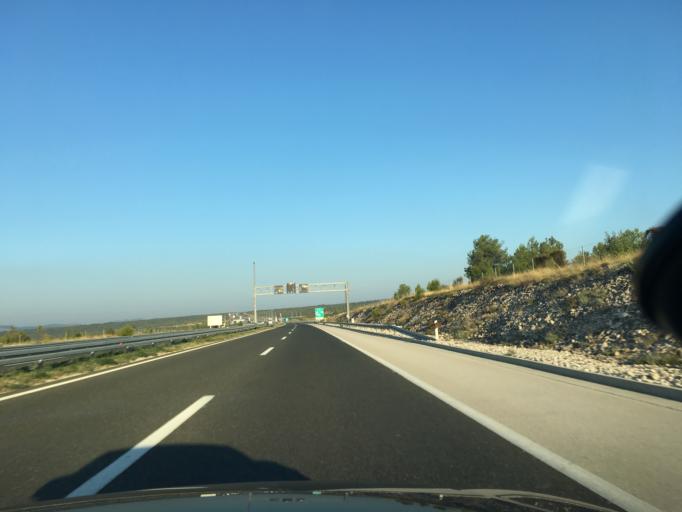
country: HR
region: Sibensko-Kniniska
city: Zaton
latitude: 43.8525
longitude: 15.8585
